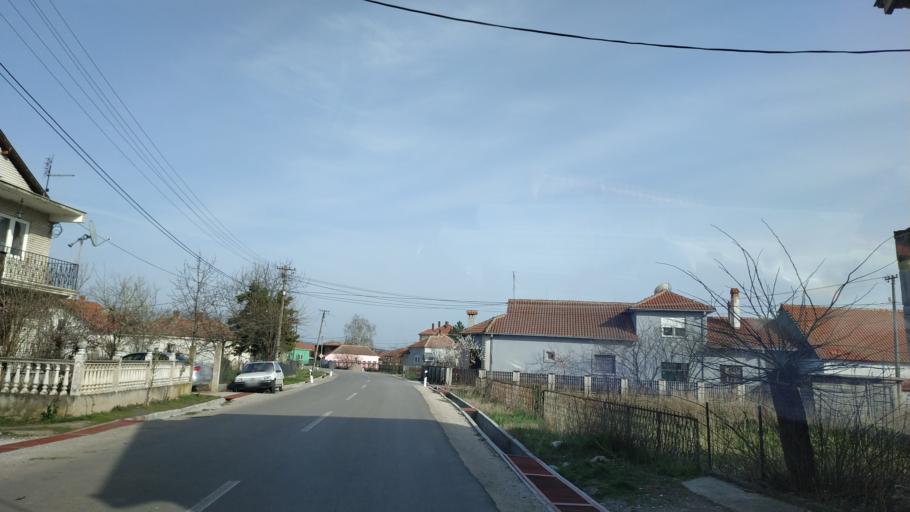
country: RS
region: Central Serbia
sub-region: Nisavski Okrug
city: Aleksinac
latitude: 43.5145
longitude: 21.6954
